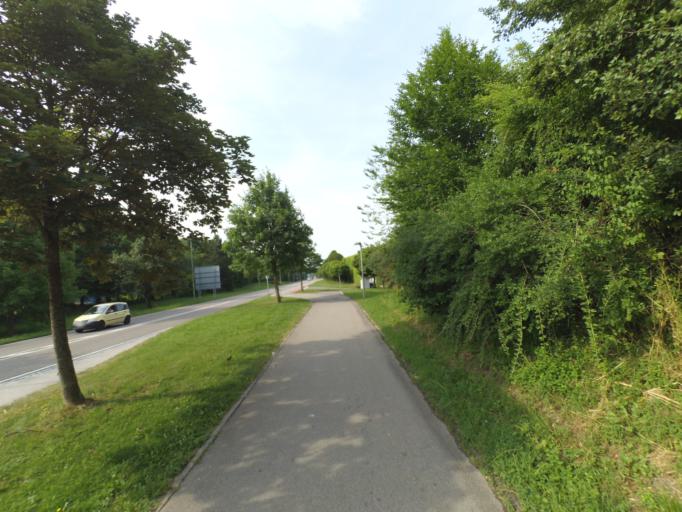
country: DE
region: Baden-Wuerttemberg
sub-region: Tuebingen Region
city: Ulm
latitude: 48.4262
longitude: 10.0069
